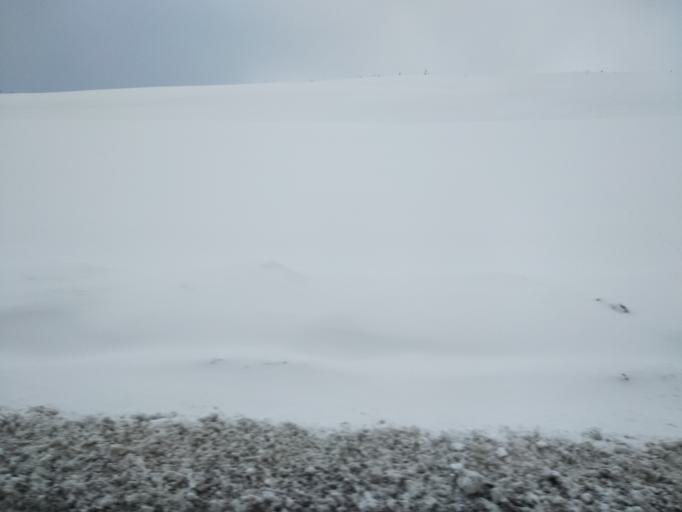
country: TR
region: Erzincan
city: Catalarmut
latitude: 39.8889
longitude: 39.3523
